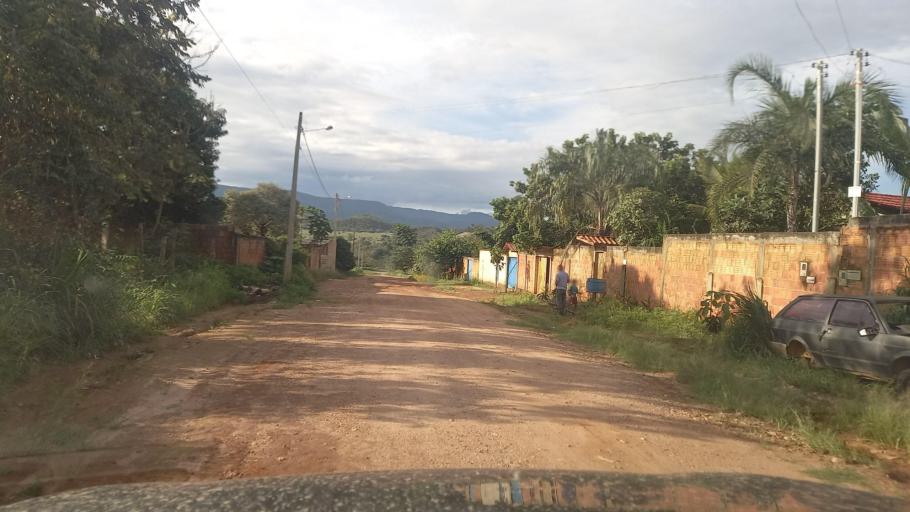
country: BR
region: Goias
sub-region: Cavalcante
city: Cavalcante
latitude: -13.7949
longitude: -47.4422
